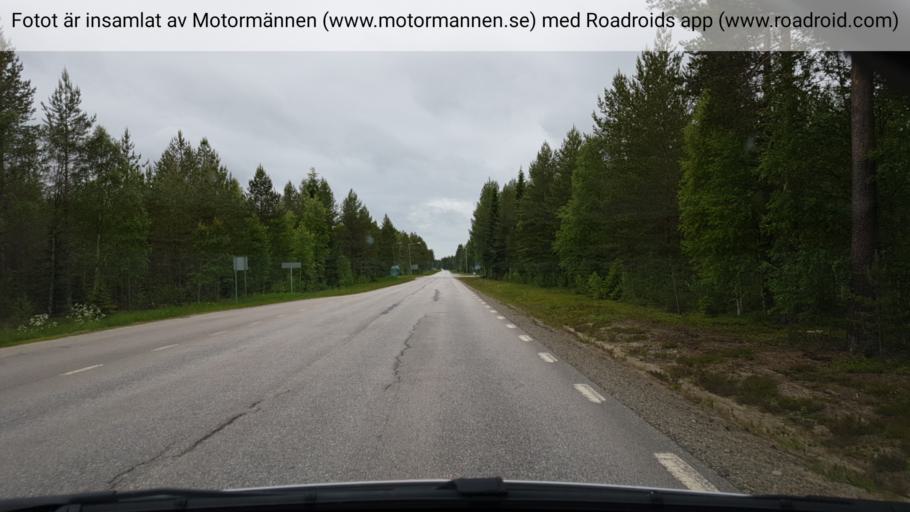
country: SE
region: Vaesterbotten
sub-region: Vindelns Kommun
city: Vindeln
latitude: 64.0826
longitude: 19.6304
